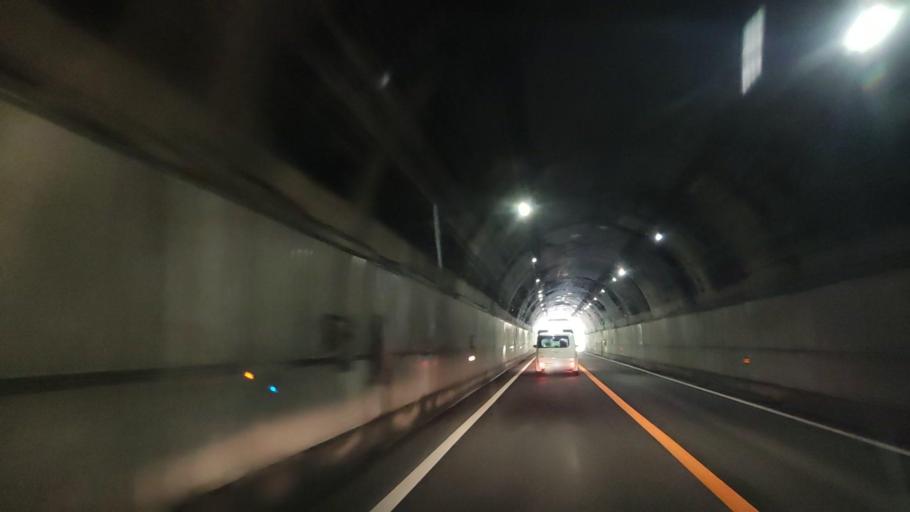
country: JP
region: Okayama
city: Niimi
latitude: 35.1849
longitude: 133.5331
